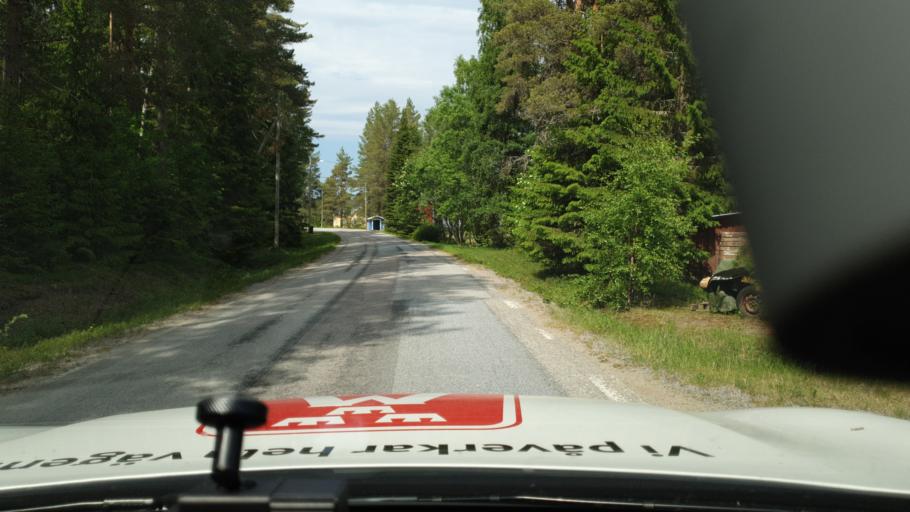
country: SE
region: Vaesterbotten
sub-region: Umea Kommun
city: Hoernefors
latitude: 63.5377
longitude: 19.7171
